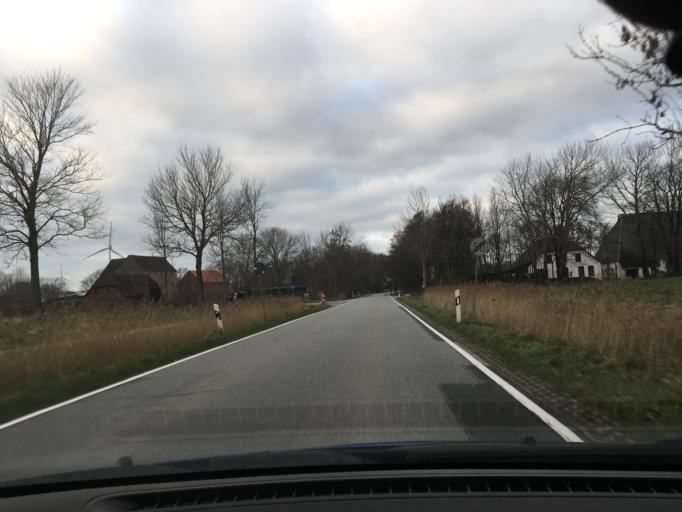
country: DE
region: Schleswig-Holstein
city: Norderwohrden
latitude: 54.1964
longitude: 9.0336
